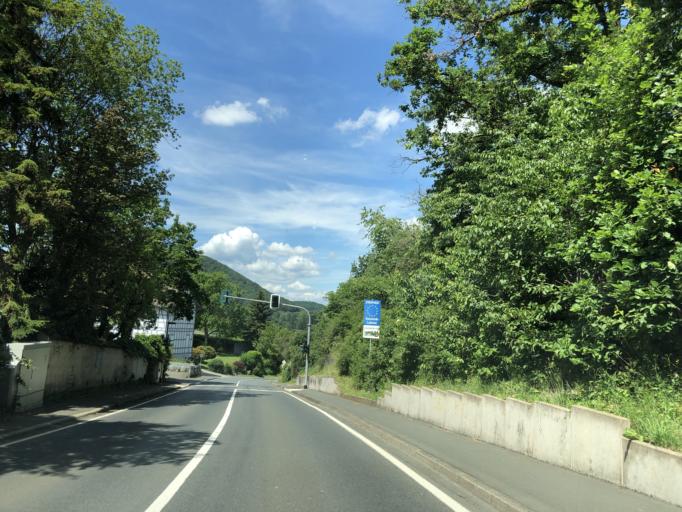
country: DE
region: Hesse
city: Wetter
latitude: 50.8459
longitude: 8.6671
